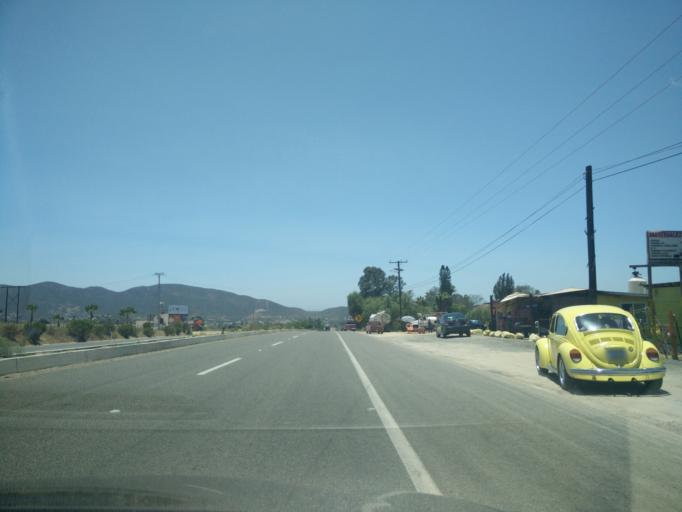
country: MX
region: Baja California
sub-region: Ensenada
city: Rancho Verde
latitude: 31.9950
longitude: -116.6398
